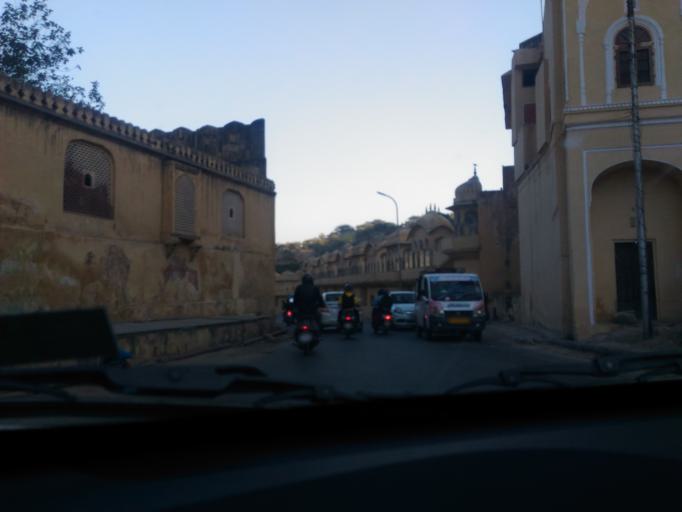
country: IN
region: Rajasthan
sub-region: Jaipur
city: Jaipur
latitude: 26.8994
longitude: 75.8546
